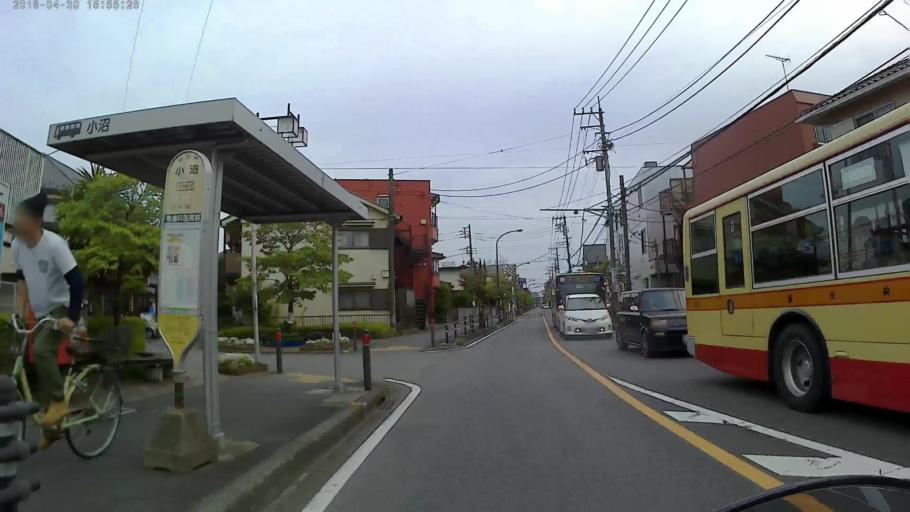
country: JP
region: Tokyo
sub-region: Machida-shi
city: Machida
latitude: 35.5391
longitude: 139.4298
